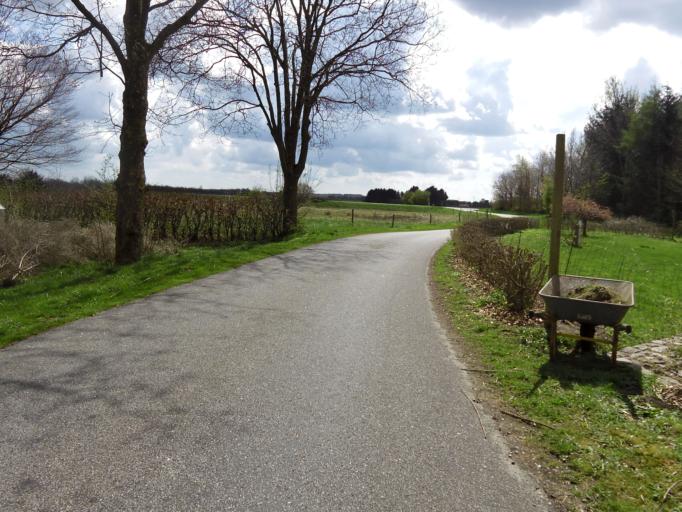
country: DK
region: South Denmark
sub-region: Tonder Kommune
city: Toftlund
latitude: 55.2040
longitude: 9.1644
